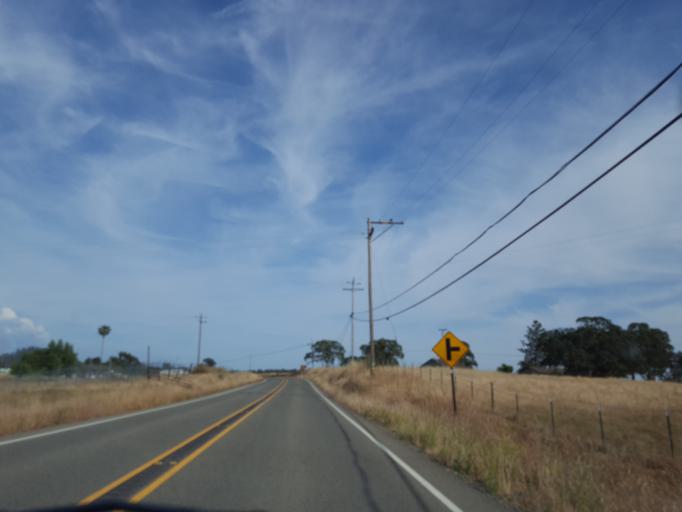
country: US
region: California
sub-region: Tuolumne County
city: Jamestown
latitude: 37.8359
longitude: -120.5038
